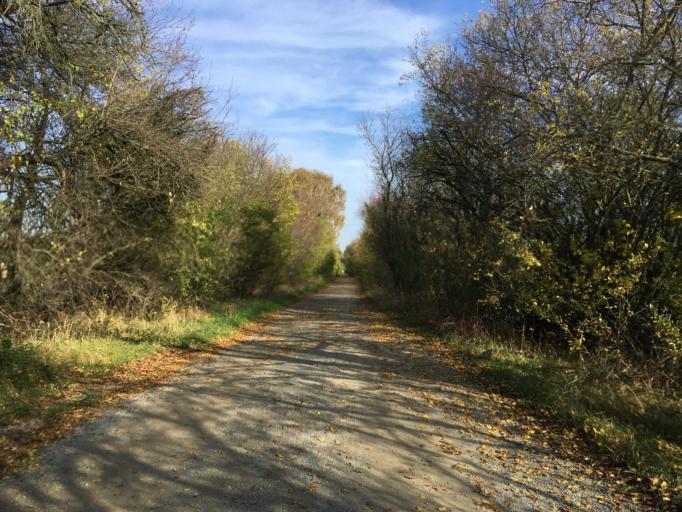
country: DE
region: Berlin
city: Buch
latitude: 52.6555
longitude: 13.4588
